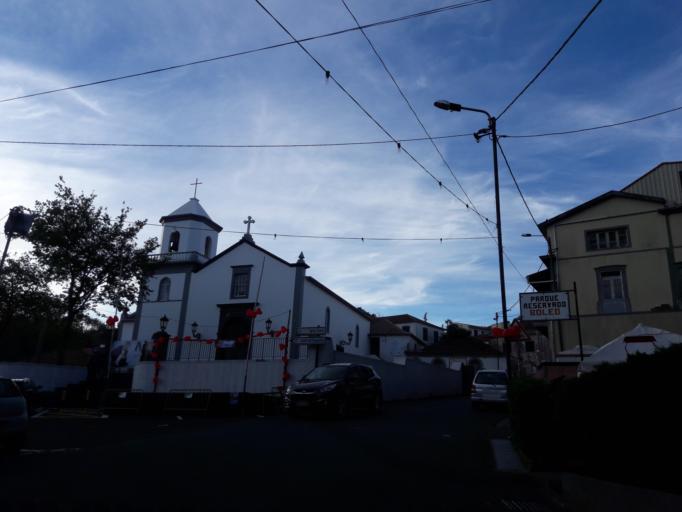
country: PT
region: Madeira
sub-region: Santa Cruz
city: Camacha
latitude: 32.6809
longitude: -16.8460
